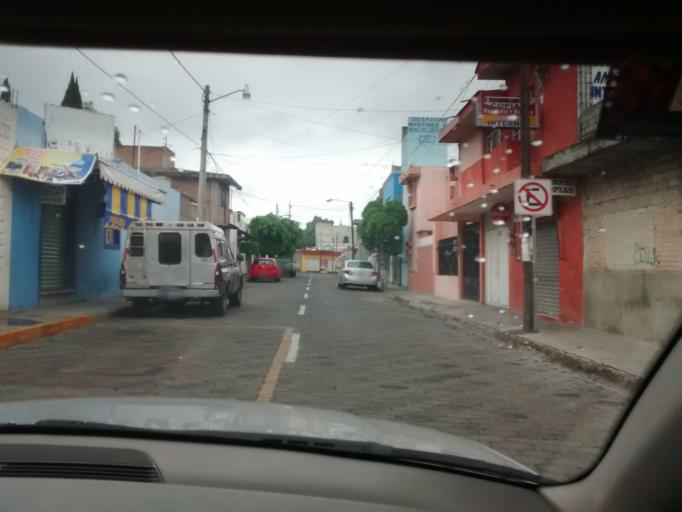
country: MX
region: Puebla
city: Tehuacan
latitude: 18.4558
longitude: -97.3951
